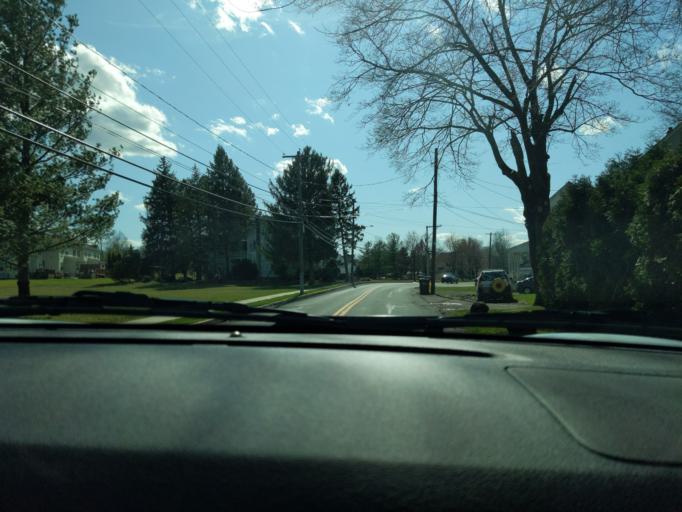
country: US
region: Pennsylvania
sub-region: Bucks County
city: Spinnerstown
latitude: 40.4366
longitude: -75.4012
